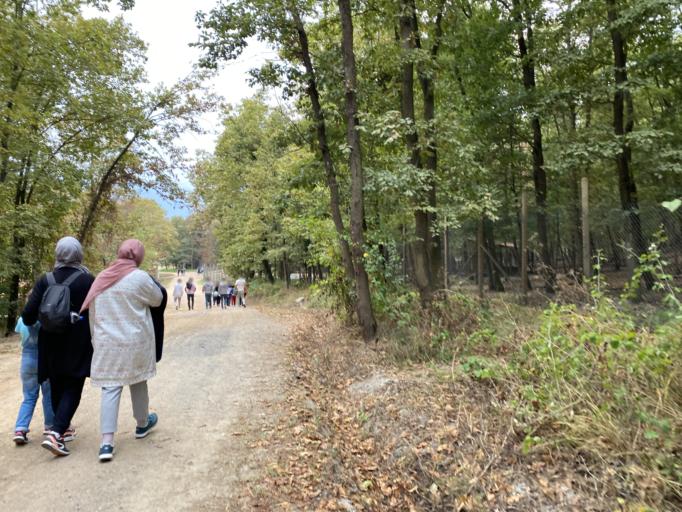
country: TR
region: Kocaeli
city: Derbent
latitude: 40.7370
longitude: 30.1611
